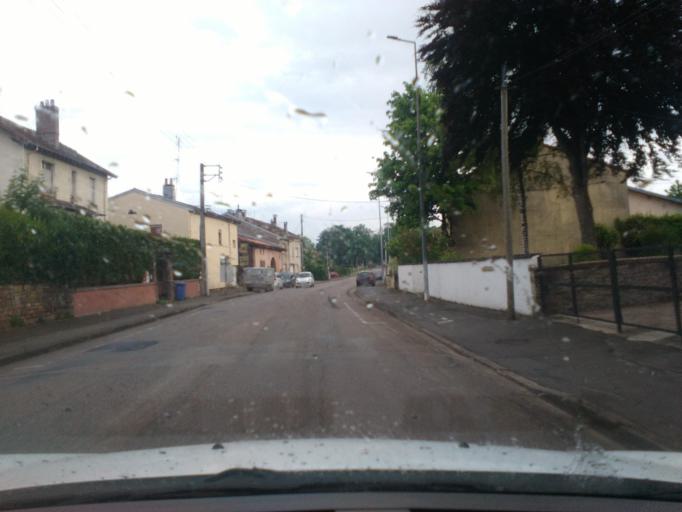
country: FR
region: Lorraine
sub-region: Departement des Vosges
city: Rambervillers
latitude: 48.3524
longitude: 6.6314
